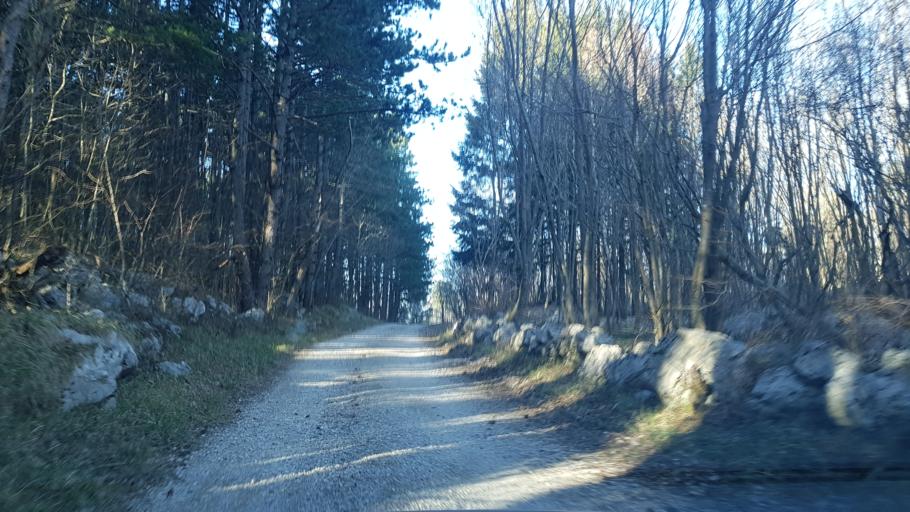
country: SI
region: Nova Gorica
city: Kromberk
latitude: 46.0175
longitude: 13.7000
